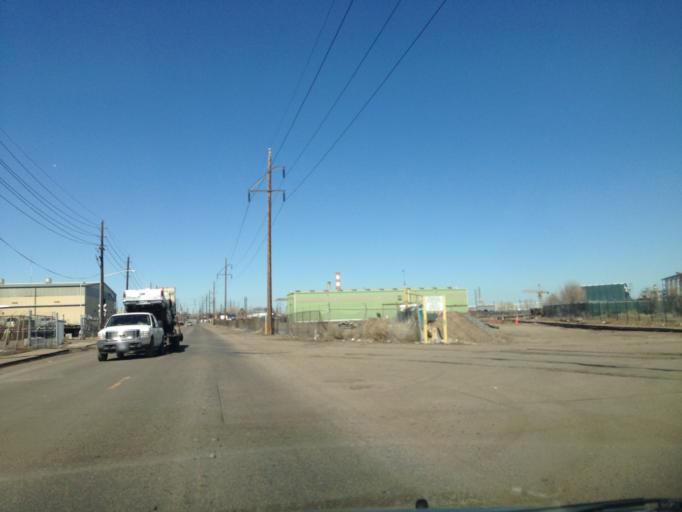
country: US
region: Colorado
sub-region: Adams County
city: Commerce City
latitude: 39.7931
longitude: -104.9688
